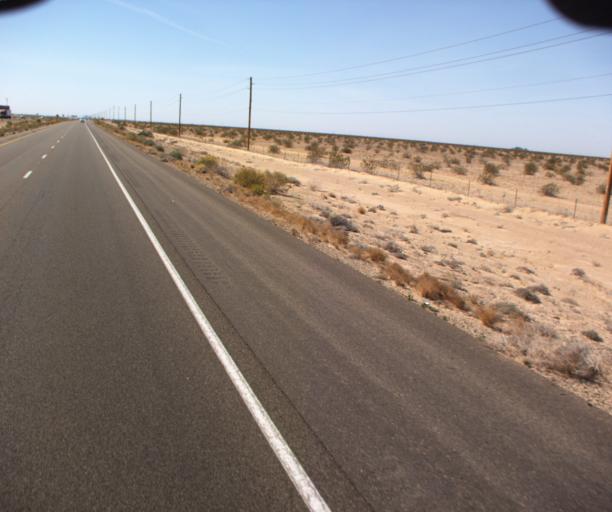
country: MX
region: Sonora
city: San Luis Rio Colorado
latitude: 32.4948
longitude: -114.6864
